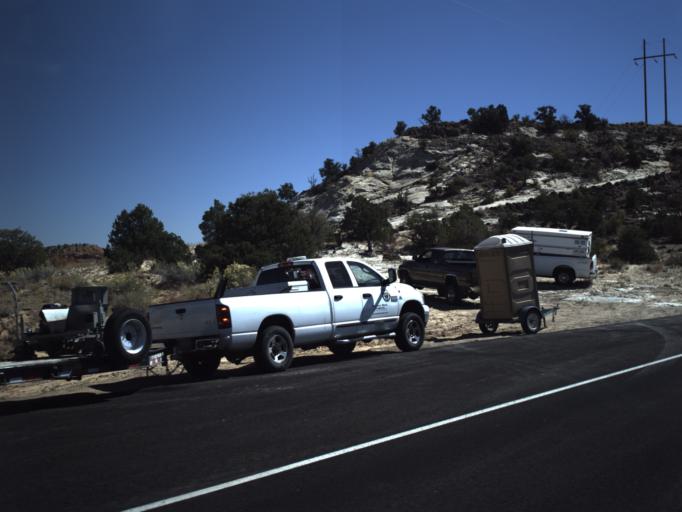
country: US
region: Utah
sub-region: Wayne County
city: Loa
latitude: 37.8270
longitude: -111.4117
